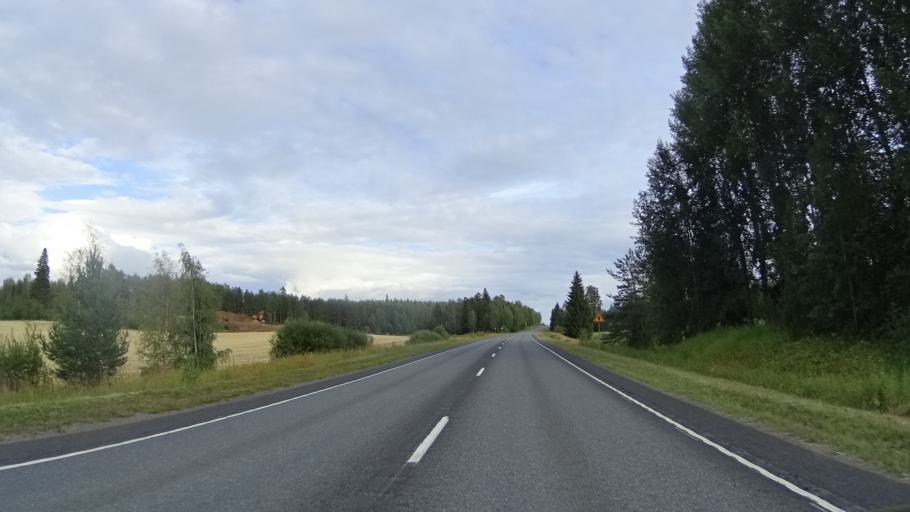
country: FI
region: Haeme
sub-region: Haemeenlinna
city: Parola
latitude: 61.0372
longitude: 24.2603
